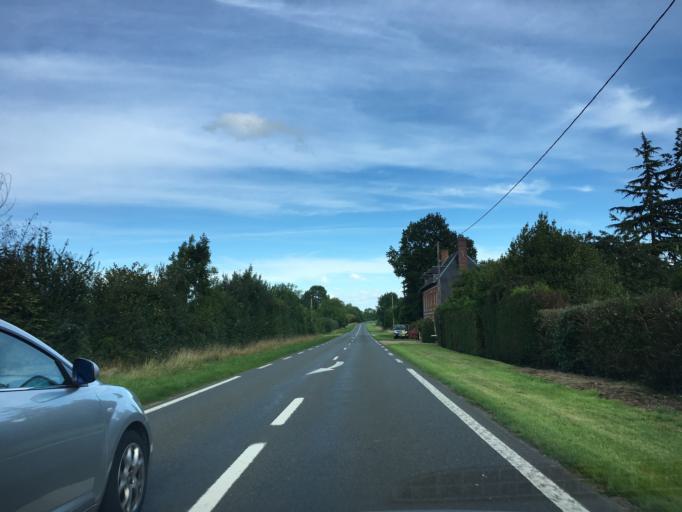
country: FR
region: Lower Normandy
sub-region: Departement du Calvados
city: Cambremer
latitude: 49.1417
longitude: 0.0853
